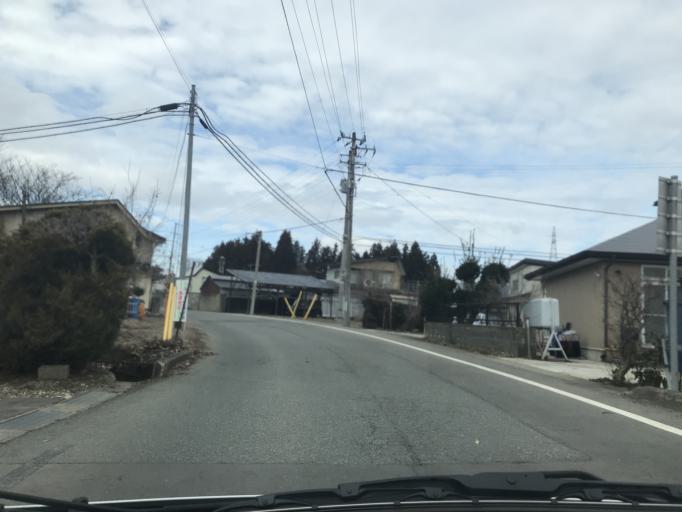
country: JP
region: Iwate
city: Kitakami
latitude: 39.3095
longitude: 140.9889
